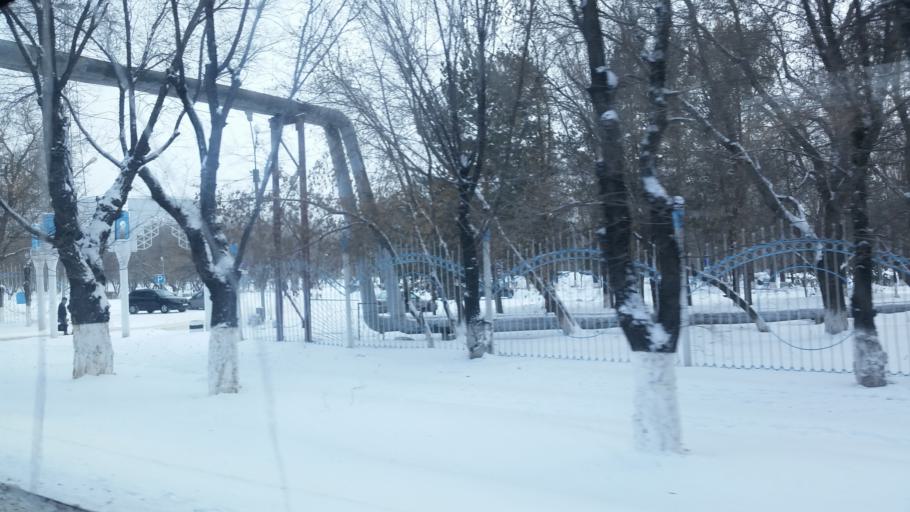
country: KZ
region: Qaraghandy
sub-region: Qaraghandy Qalasy
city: Karagandy
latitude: 49.8125
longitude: 73.0729
